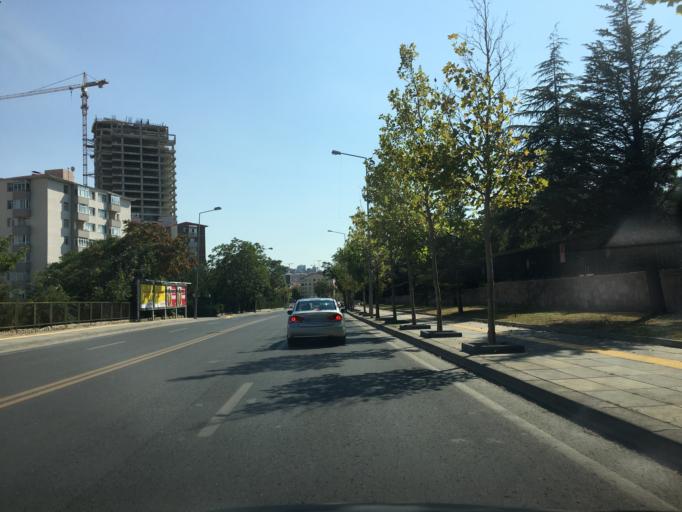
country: TR
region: Ankara
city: Cankaya
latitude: 39.8811
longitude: 32.8662
